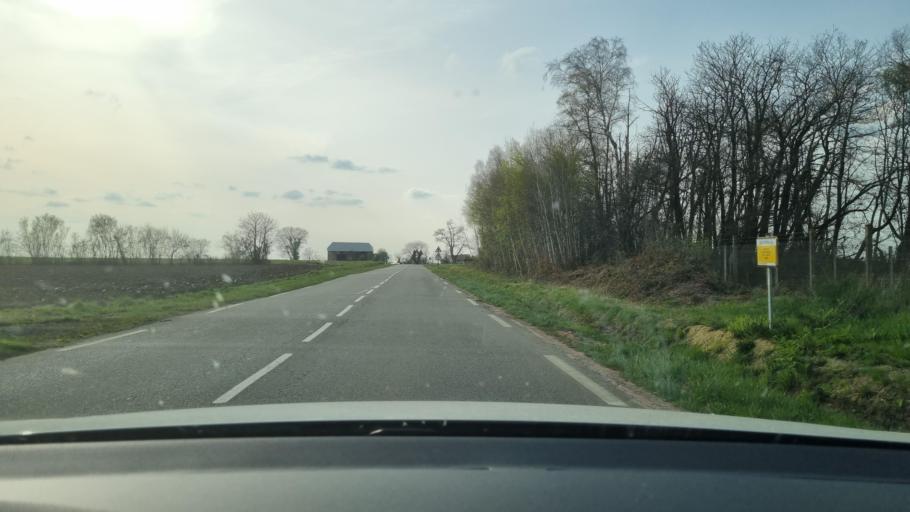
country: FR
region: Aquitaine
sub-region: Departement des Pyrenees-Atlantiques
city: Ger
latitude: 43.3769
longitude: -0.1000
